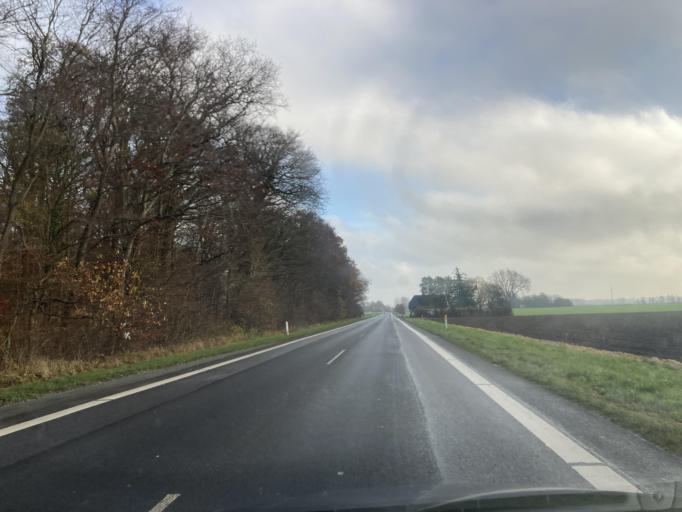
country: DK
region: Zealand
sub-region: Lolland Kommune
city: Maribo
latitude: 54.8141
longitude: 11.3934
